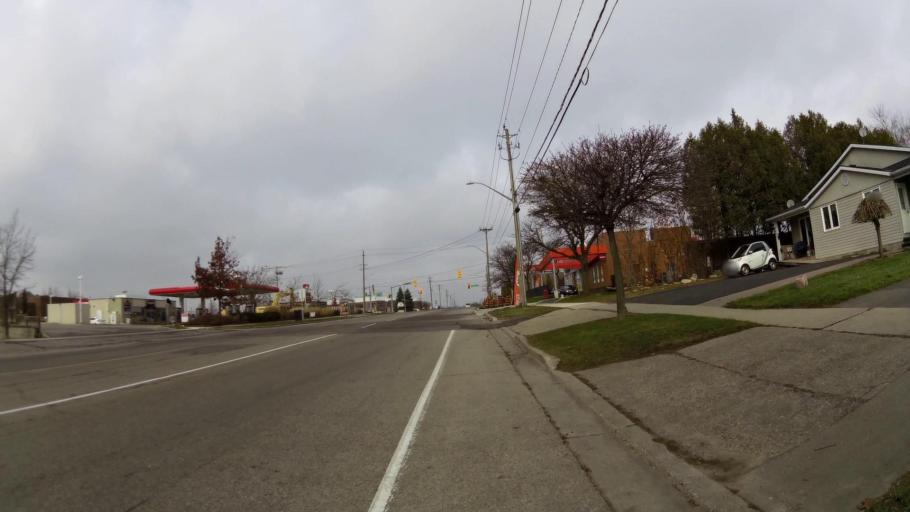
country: CA
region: Ontario
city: Kitchener
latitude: 43.4221
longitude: -80.4868
